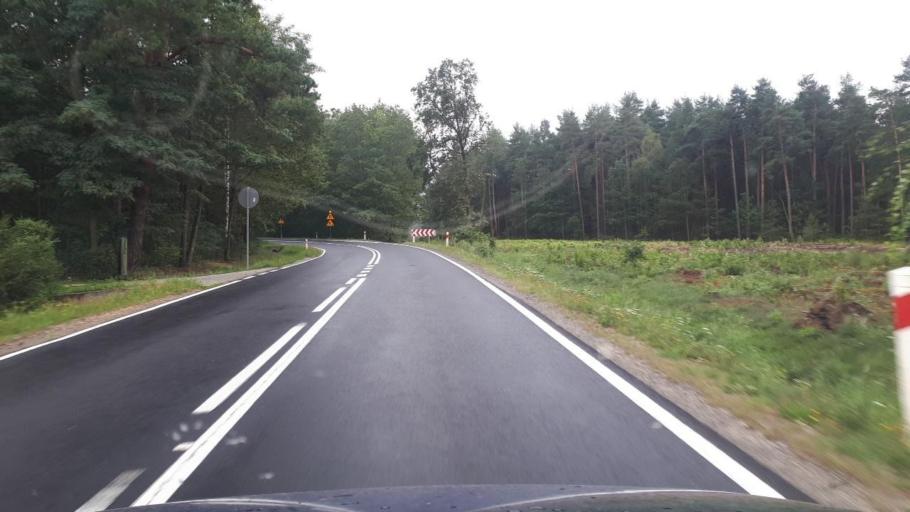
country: PL
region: Silesian Voivodeship
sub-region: Powiat lubliniecki
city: Sierakow Slaski
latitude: 50.8205
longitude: 18.5332
